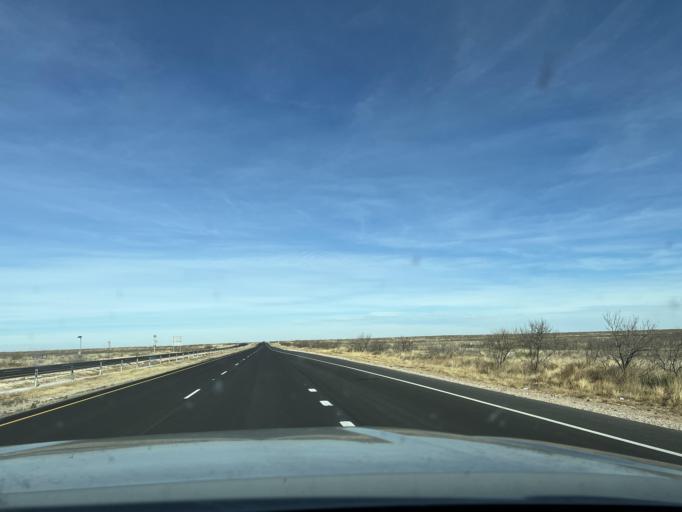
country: US
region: Texas
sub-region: Ector County
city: Gardendale
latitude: 32.0289
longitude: -102.4320
